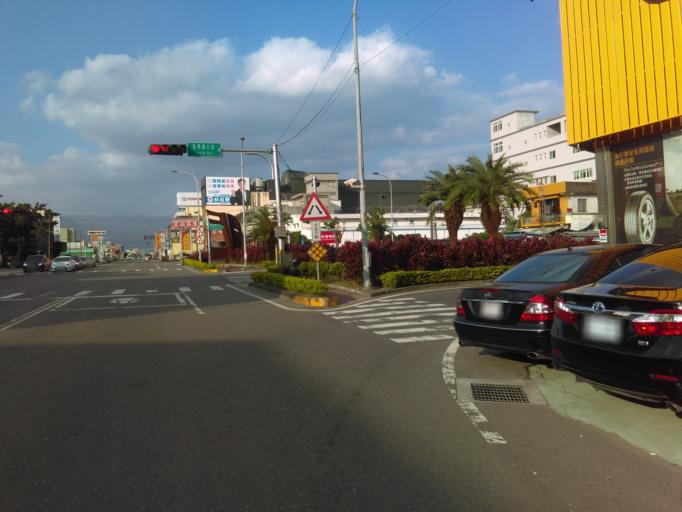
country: TW
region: Taiwan
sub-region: Yilan
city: Yilan
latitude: 24.7719
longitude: 121.7575
